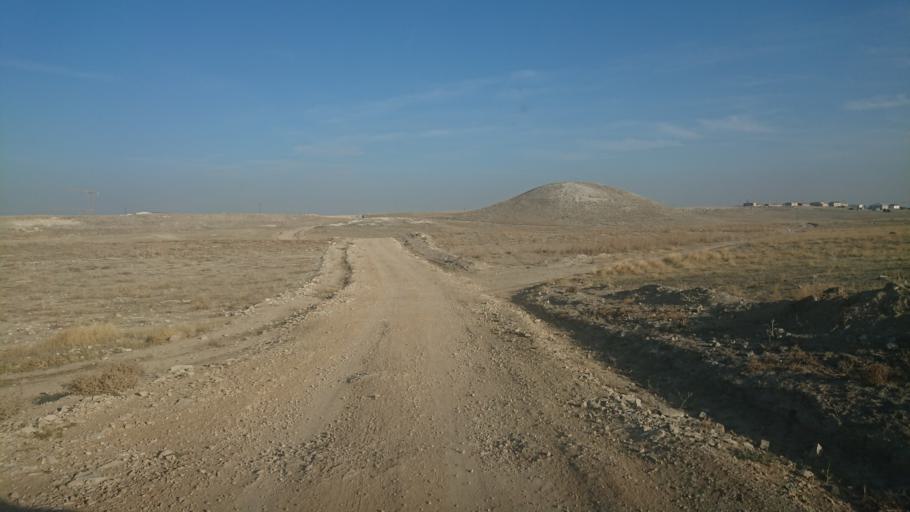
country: TR
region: Aksaray
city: Sultanhani
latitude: 38.1451
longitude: 33.5809
